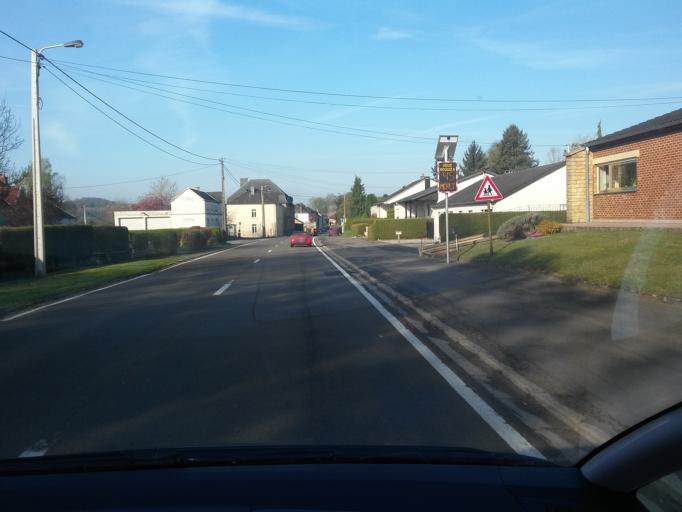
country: BE
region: Wallonia
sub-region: Province du Luxembourg
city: Virton
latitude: 49.5818
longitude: 5.5895
